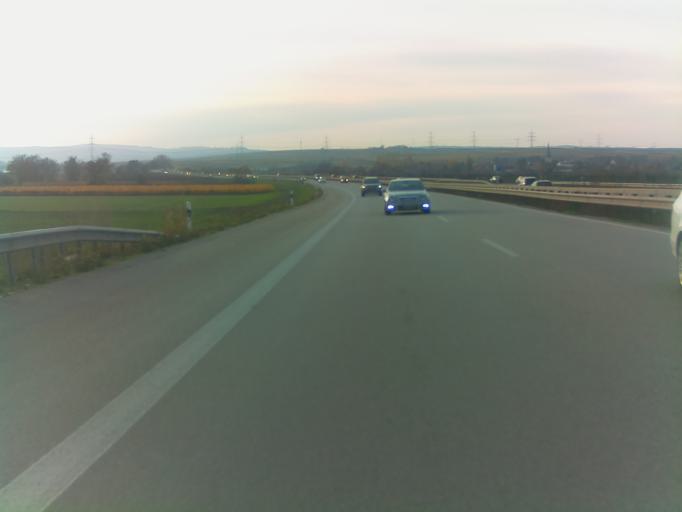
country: DE
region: Rheinland-Pfalz
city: Gerolsheim
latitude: 49.5519
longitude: 8.2563
